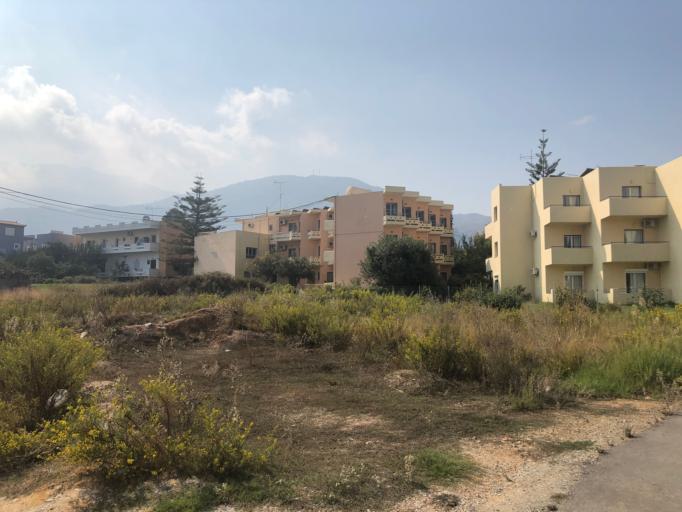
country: GR
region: Crete
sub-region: Nomos Chanias
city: Georgioupolis
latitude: 35.3603
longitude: 24.2611
